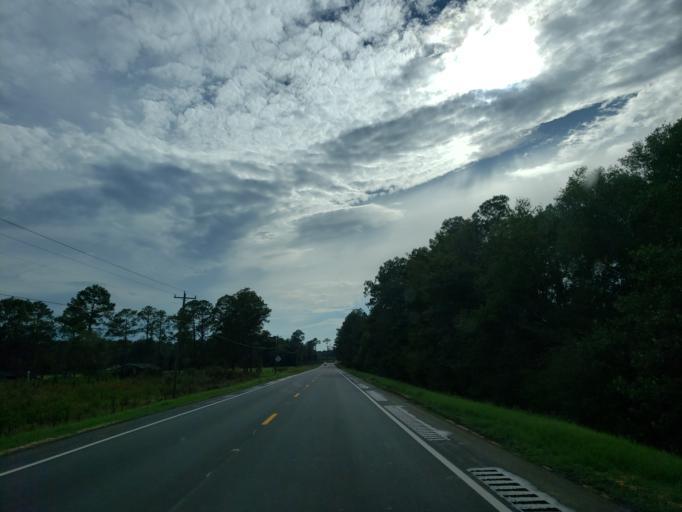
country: US
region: Georgia
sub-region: Irwin County
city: Ocilla
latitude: 31.5645
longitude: -83.3206
